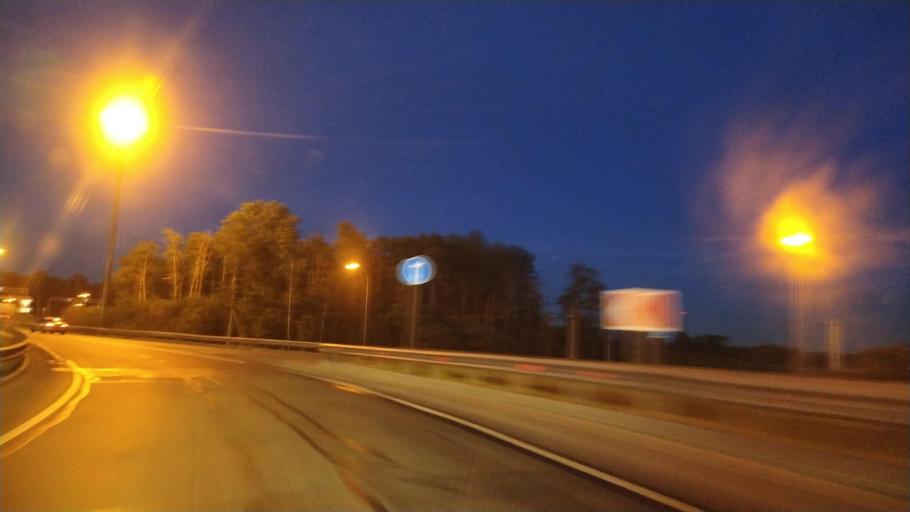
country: RU
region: Leningrad
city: Rybatskoye
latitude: 59.8894
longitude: 30.5204
